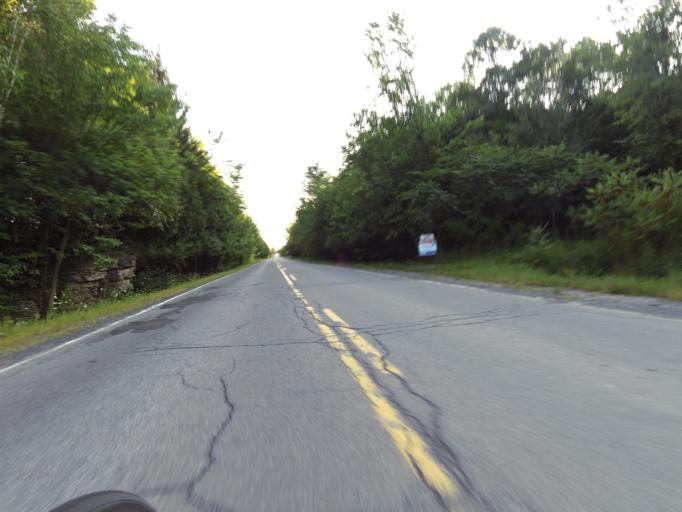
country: CA
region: Ontario
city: Bells Corners
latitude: 45.3808
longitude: -75.9507
